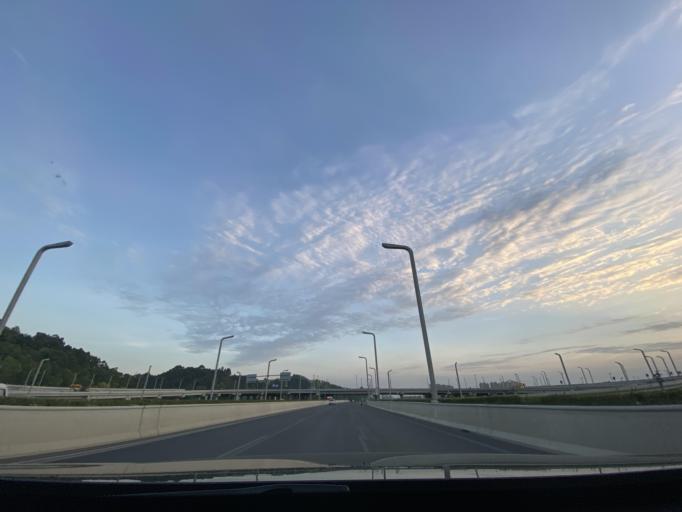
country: CN
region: Sichuan
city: Longquan
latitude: 30.5964
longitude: 104.3064
